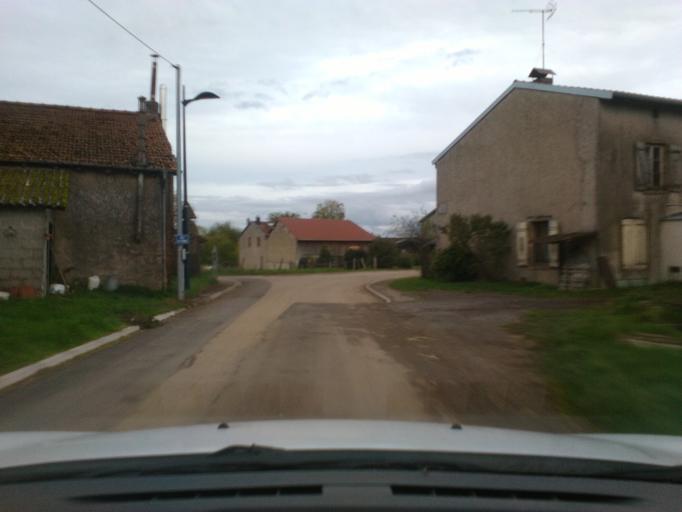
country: FR
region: Lorraine
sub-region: Departement des Vosges
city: Mirecourt
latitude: 48.3360
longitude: 6.0957
